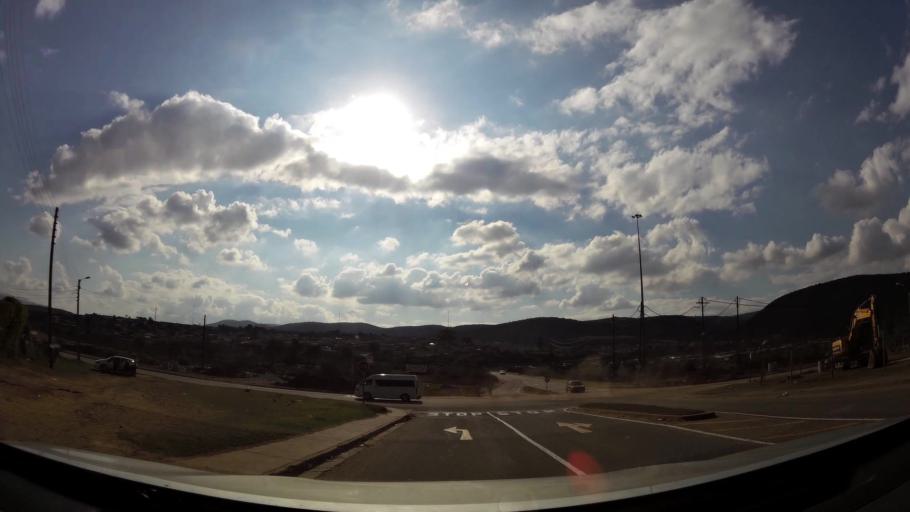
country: ZA
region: Eastern Cape
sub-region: Nelson Mandela Bay Metropolitan Municipality
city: Uitenhage
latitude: -33.7336
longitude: 25.3683
